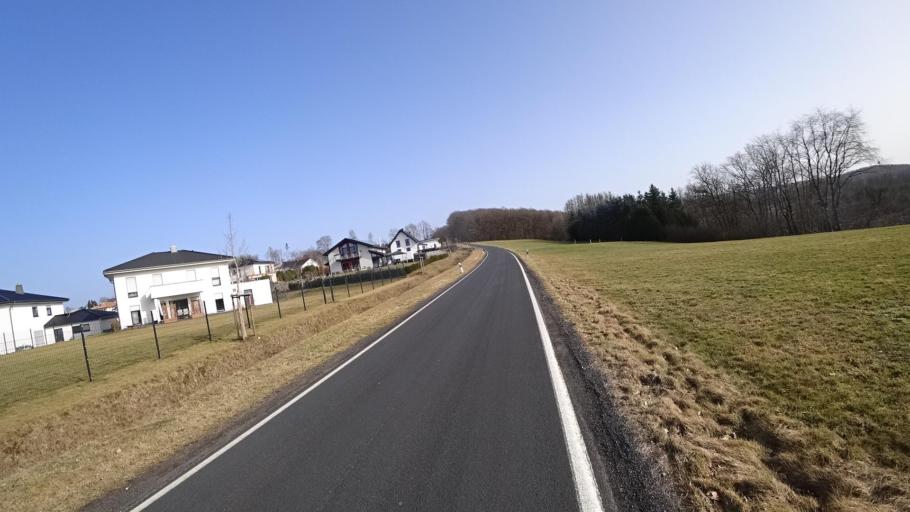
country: DE
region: Rheinland-Pfalz
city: Wissen
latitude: 50.7710
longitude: 7.7650
